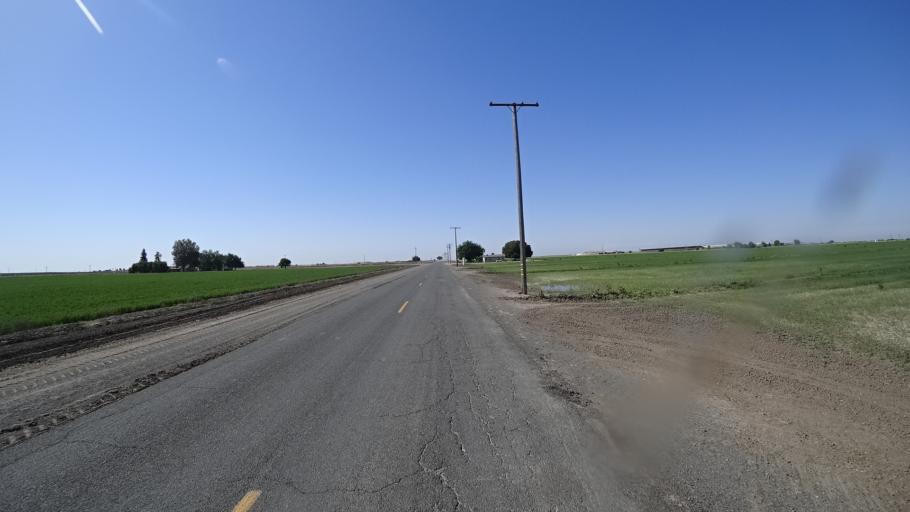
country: US
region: California
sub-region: Kings County
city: Home Garden
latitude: 36.2302
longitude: -119.5473
